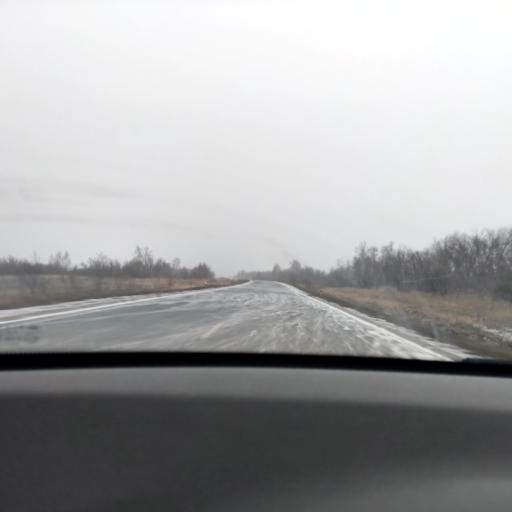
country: RU
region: Samara
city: Novokuybyshevsk
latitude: 52.9197
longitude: 49.9237
